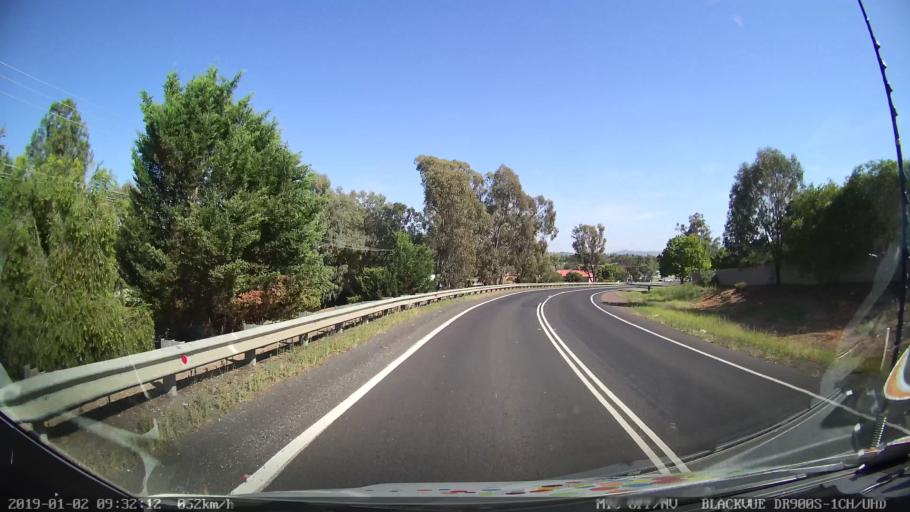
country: AU
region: New South Wales
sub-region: Tumut Shire
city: Tumut
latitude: -35.3137
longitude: 148.2312
